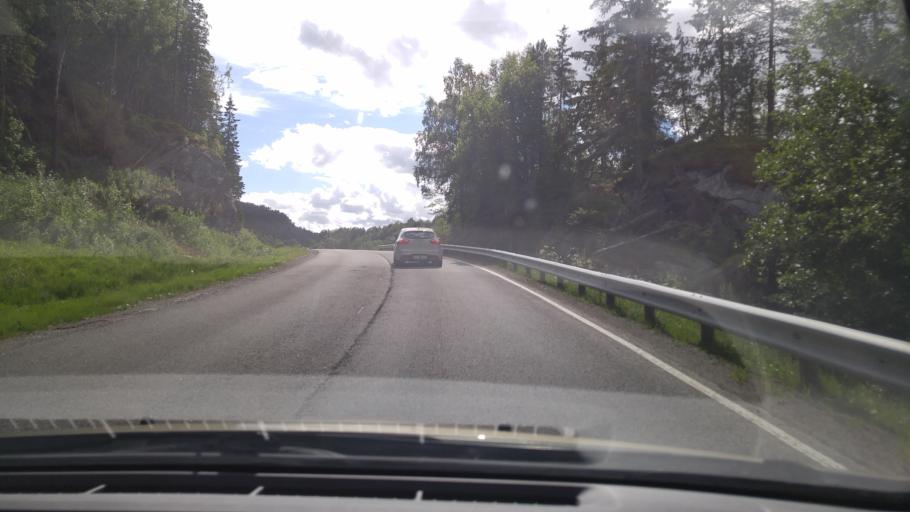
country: NO
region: Nord-Trondelag
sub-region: Namdalseid
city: Namdalseid
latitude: 64.3654
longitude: 11.3192
